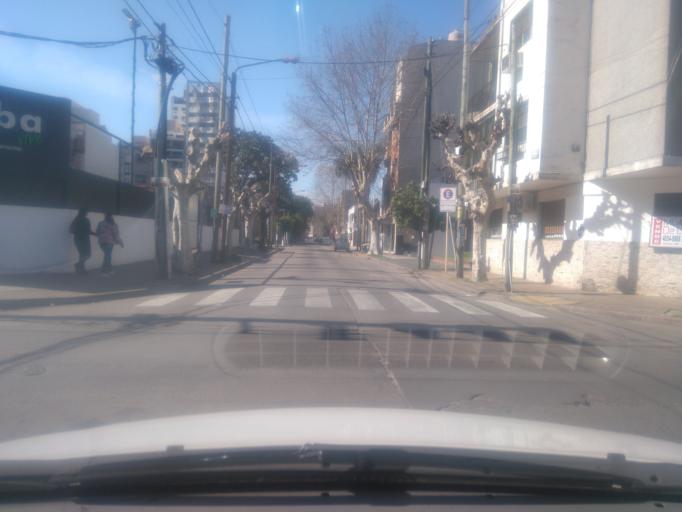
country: AR
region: Buenos Aires
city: San Justo
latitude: -34.6456
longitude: -58.5664
